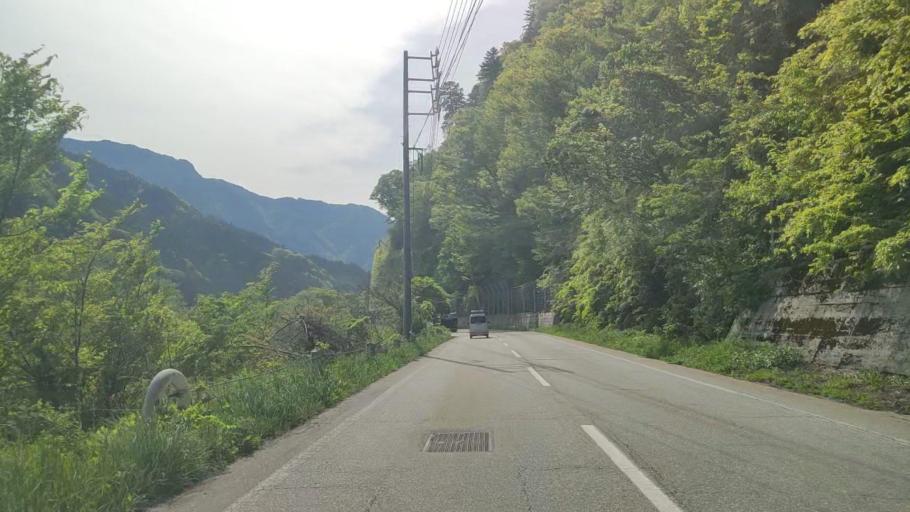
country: JP
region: Gifu
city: Takayama
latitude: 36.2590
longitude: 137.4604
